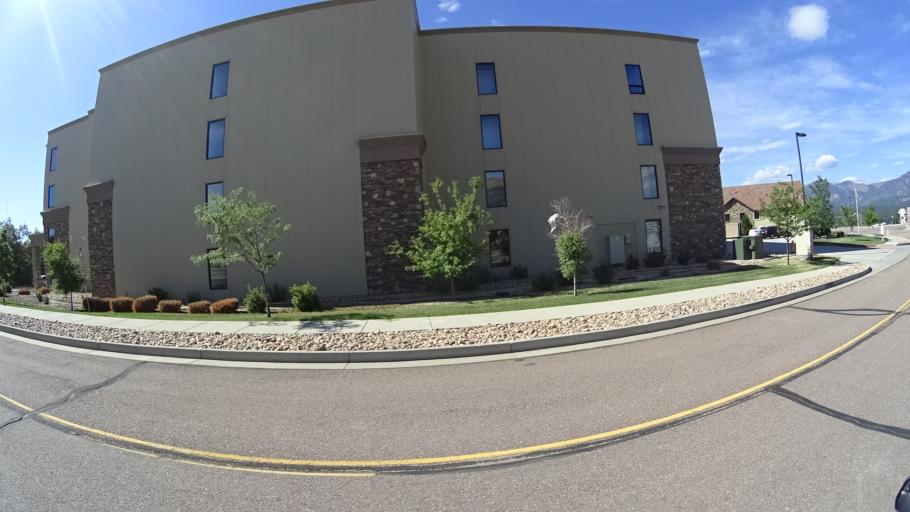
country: US
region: Colorado
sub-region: El Paso County
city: Gleneagle
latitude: 39.0213
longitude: -104.8121
